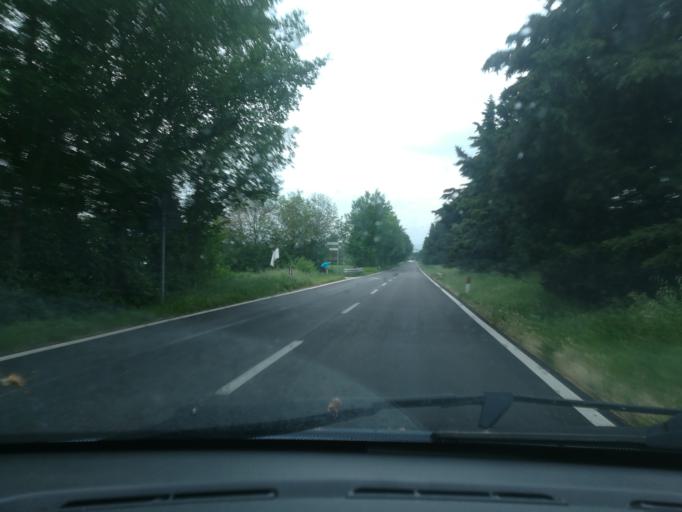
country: IT
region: The Marches
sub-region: Provincia di Macerata
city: Treia
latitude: 43.2740
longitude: 13.2905
